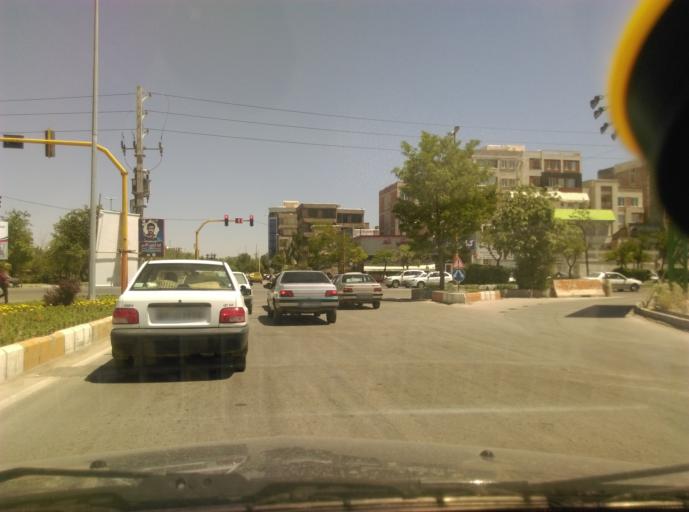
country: IR
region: Ardabil
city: Ardabil
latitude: 38.2245
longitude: 48.2799
